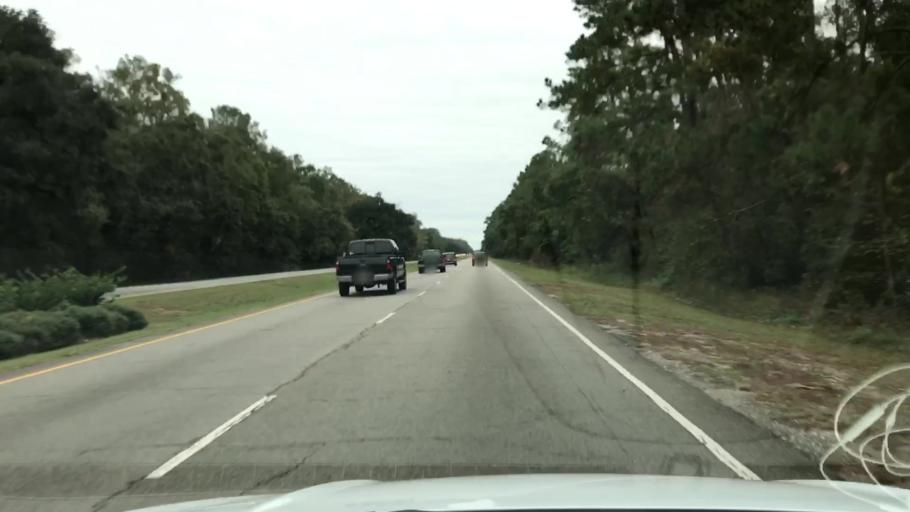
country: US
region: South Carolina
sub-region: Georgetown County
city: Murrells Inlet
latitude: 33.5018
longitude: -79.0819
